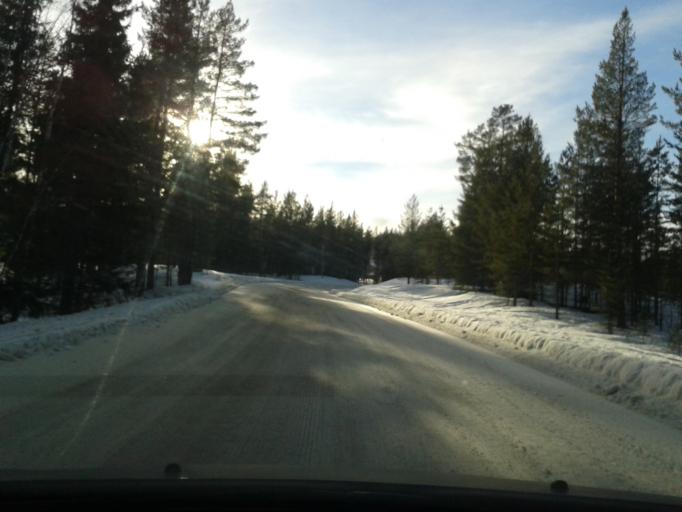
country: SE
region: Vaesternorrland
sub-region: OErnskoeldsviks Kommun
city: Bredbyn
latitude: 63.6742
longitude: 17.8066
